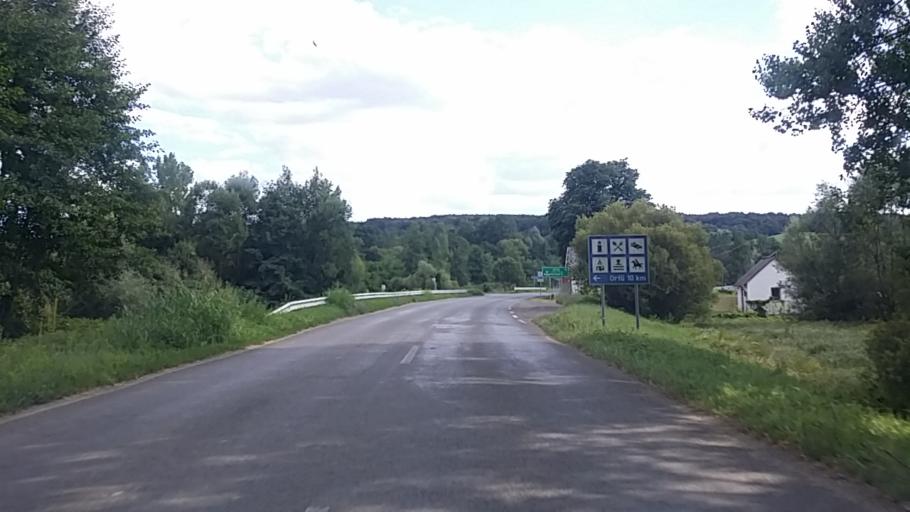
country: HU
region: Baranya
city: Sasd
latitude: 46.2118
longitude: 18.1045
